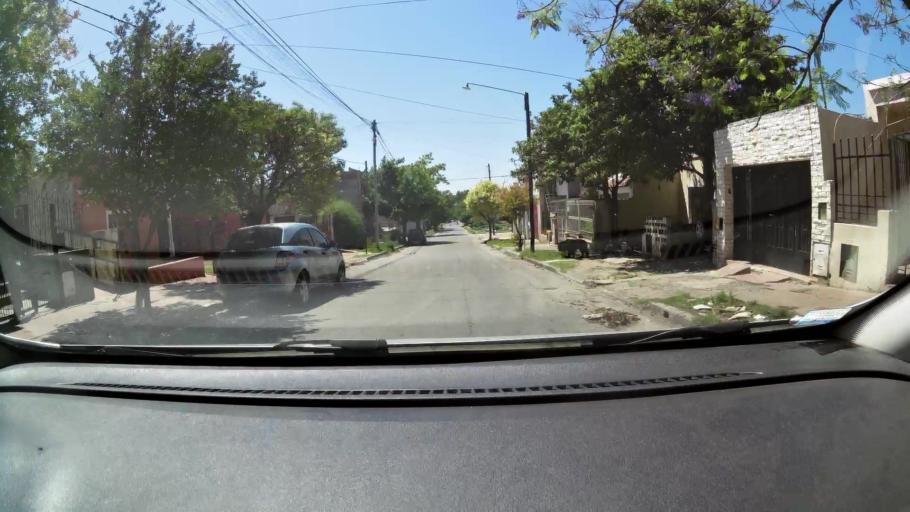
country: AR
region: Cordoba
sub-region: Departamento de Capital
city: Cordoba
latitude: -31.4335
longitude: -64.2055
